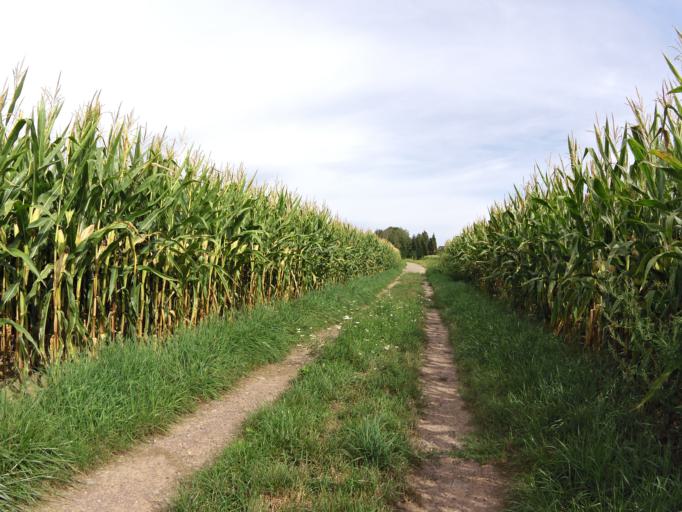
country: DE
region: Baden-Wuerttemberg
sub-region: Freiburg Region
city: Lahr
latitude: 48.3566
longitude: 7.8372
